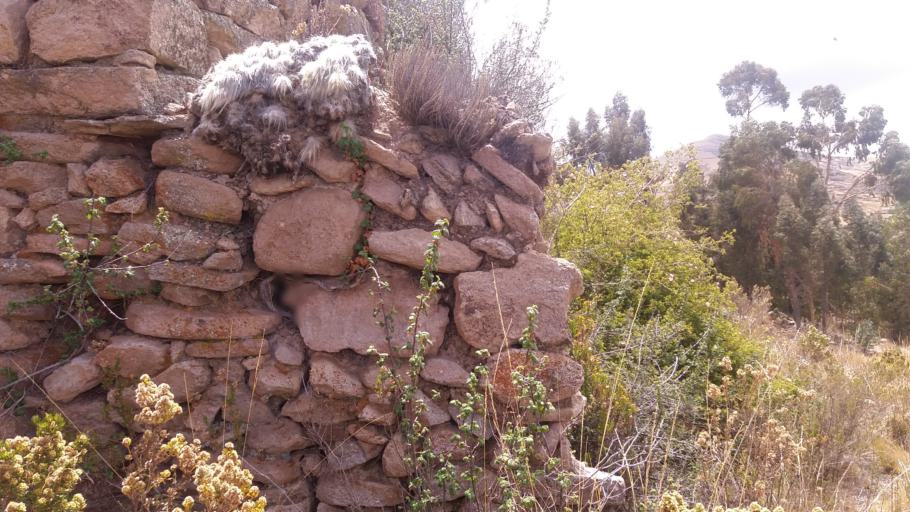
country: PE
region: Puno
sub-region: Yunguyo
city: Yunguyo
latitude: -16.1837
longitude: -69.0854
